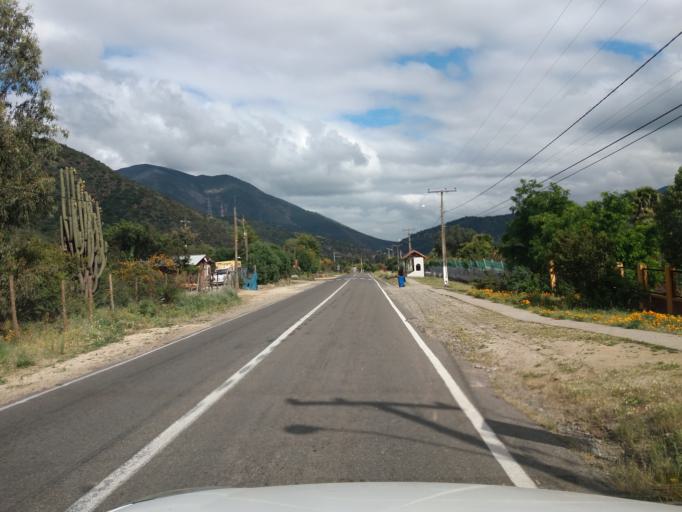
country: CL
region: Valparaiso
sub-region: Provincia de Marga Marga
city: Limache
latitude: -33.0578
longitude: -71.0839
